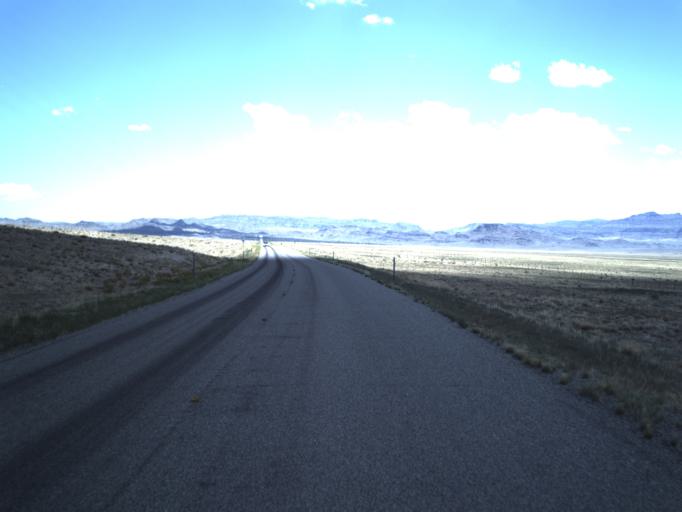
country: US
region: Utah
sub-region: Beaver County
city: Milford
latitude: 39.0405
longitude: -113.8123
